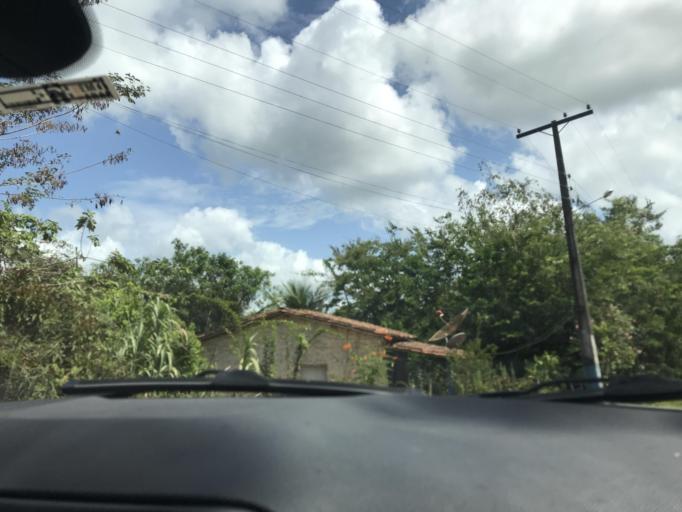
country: BR
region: Bahia
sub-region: Entre Rios
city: Entre Rios
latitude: -12.1877
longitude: -38.0482
